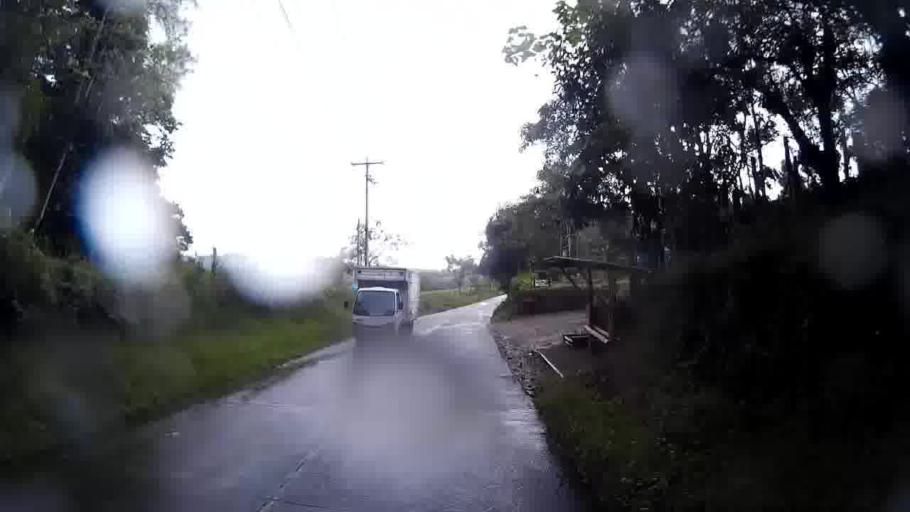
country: CO
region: Quindio
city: Filandia
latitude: 4.6888
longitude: -75.6134
